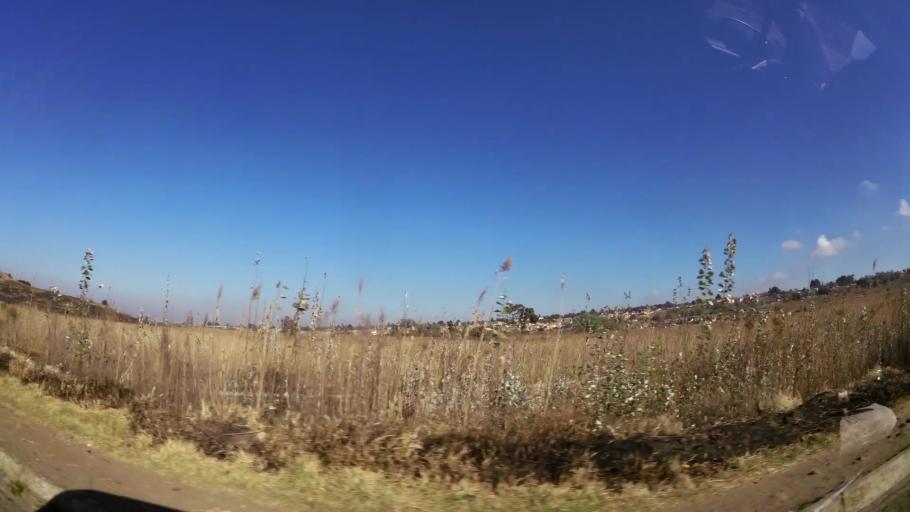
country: ZA
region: Gauteng
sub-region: City of Johannesburg Metropolitan Municipality
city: Roodepoort
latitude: -26.1570
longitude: 27.8437
